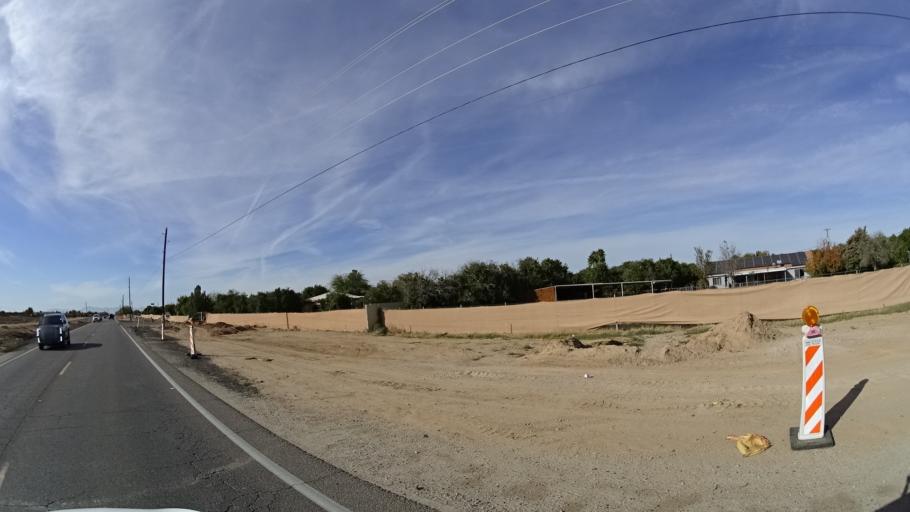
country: US
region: Arizona
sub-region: Maricopa County
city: Queen Creek
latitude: 33.2196
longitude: -111.6912
